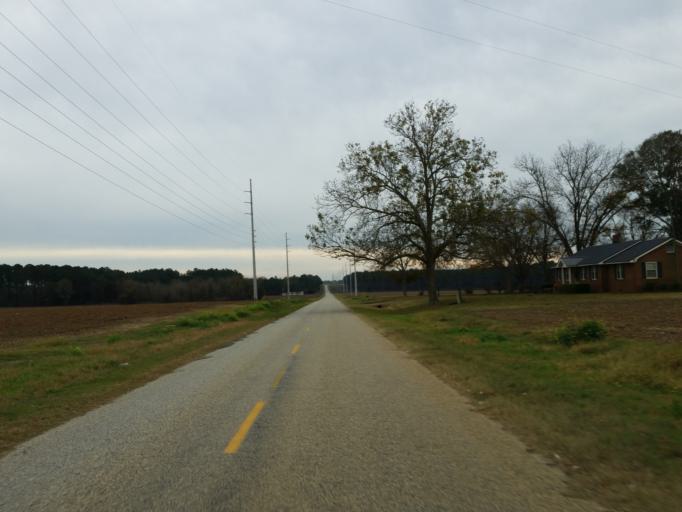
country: US
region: Georgia
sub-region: Dooly County
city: Vienna
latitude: 32.1431
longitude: -83.7611
